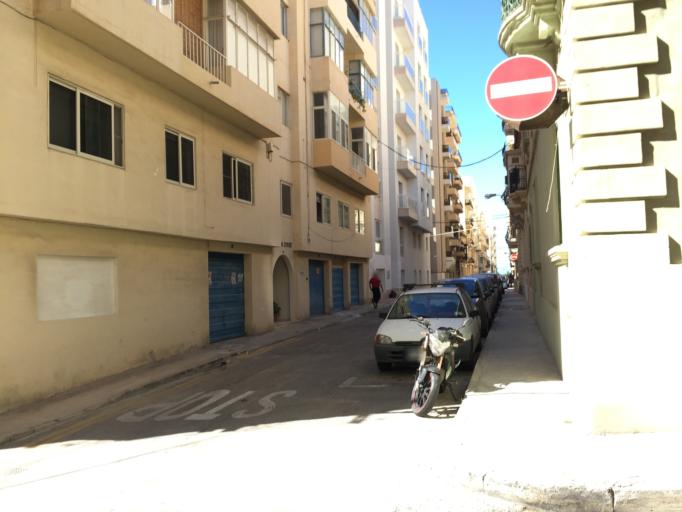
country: MT
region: Tas-Sliema
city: Sliema
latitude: 35.9152
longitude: 14.4987
